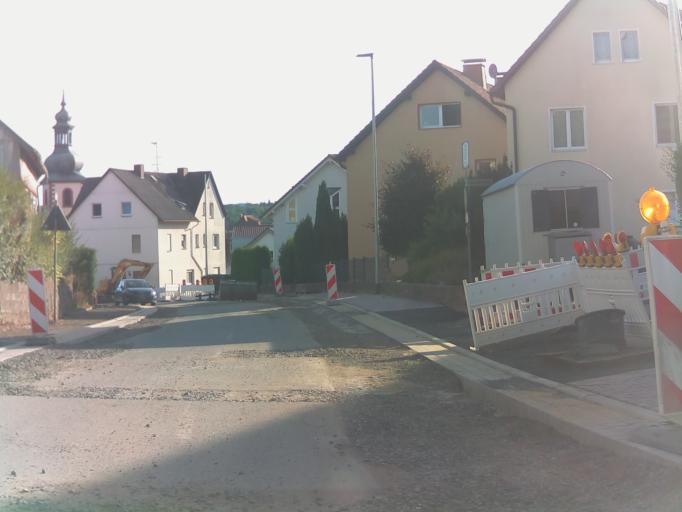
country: DE
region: Hesse
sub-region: Regierungsbezirk Kassel
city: Flieden
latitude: 50.4247
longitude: 9.5676
